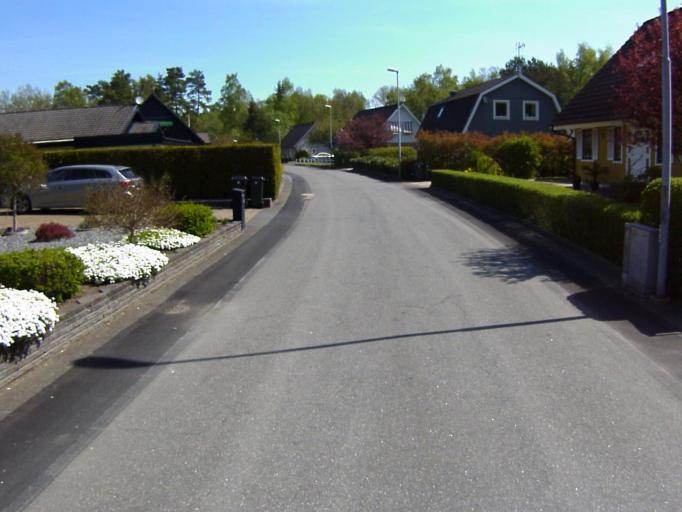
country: SE
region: Skane
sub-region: Kristianstads Kommun
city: Onnestad
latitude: 55.9396
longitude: 13.9833
